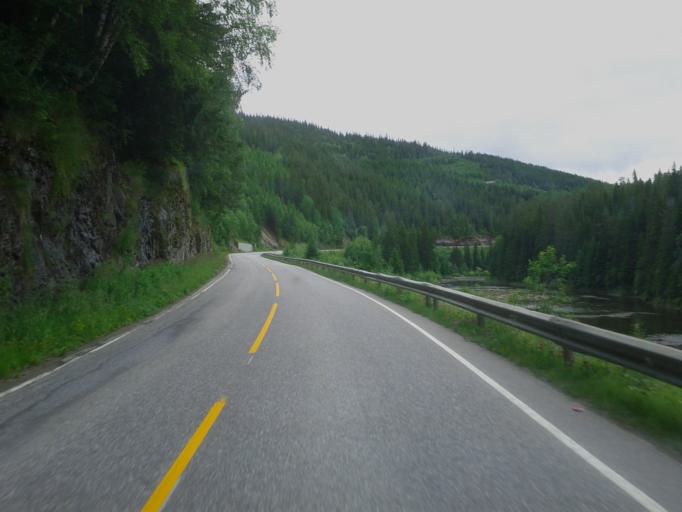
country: NO
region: Sor-Trondelag
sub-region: Holtalen
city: Alen
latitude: 62.8699
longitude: 11.2055
